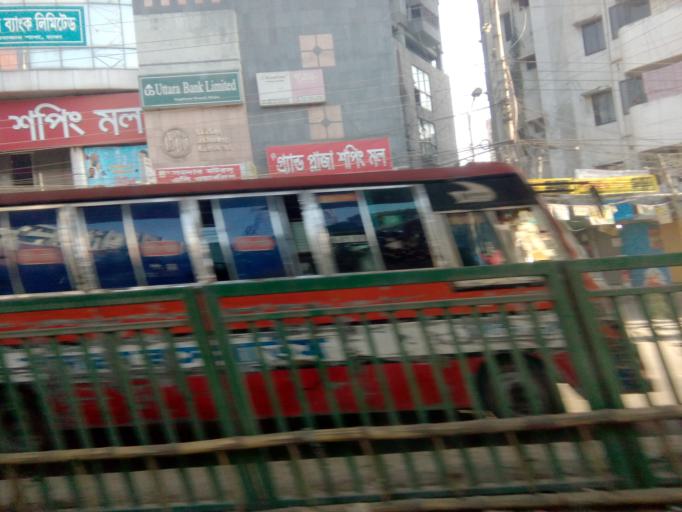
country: BD
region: Dhaka
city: Paltan
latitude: 23.7483
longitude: 90.4091
